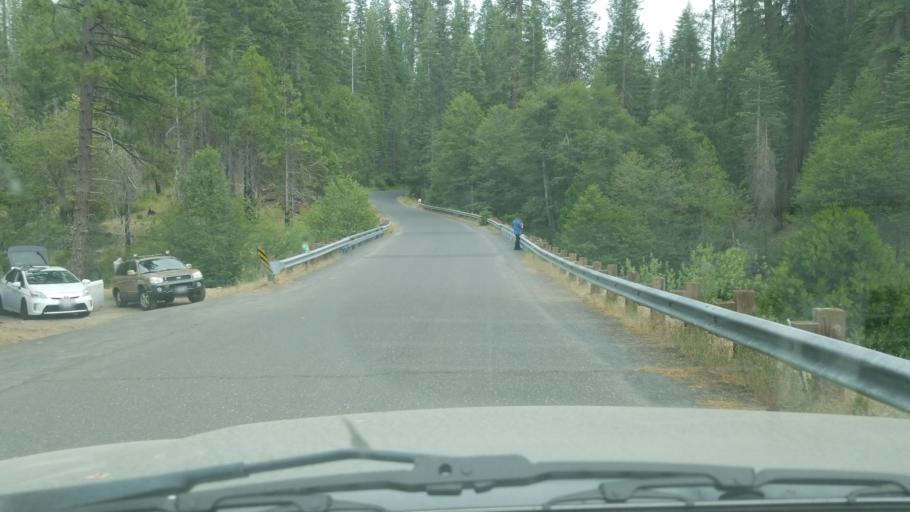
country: US
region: California
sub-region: Mariposa County
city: Yosemite Valley
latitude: 37.8567
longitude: -119.8655
